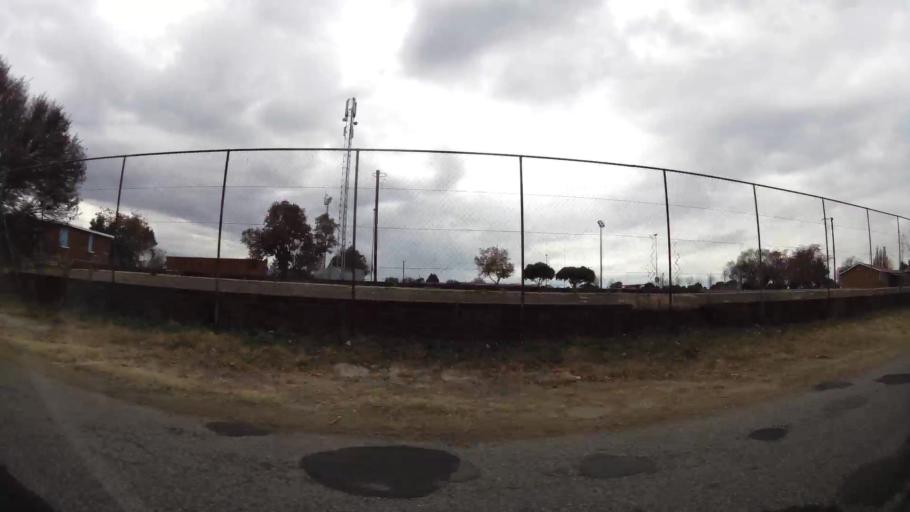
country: ZA
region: Orange Free State
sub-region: Fezile Dabi District Municipality
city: Kroonstad
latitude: -27.6403
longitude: 27.2307
